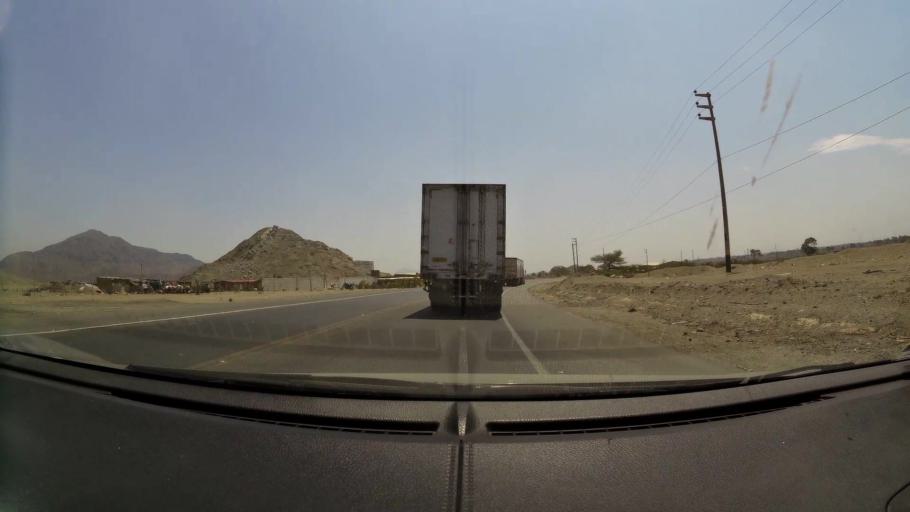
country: PE
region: La Libertad
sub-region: Provincia de Pacasmayo
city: Guadalupe
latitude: -7.2587
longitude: -79.4906
